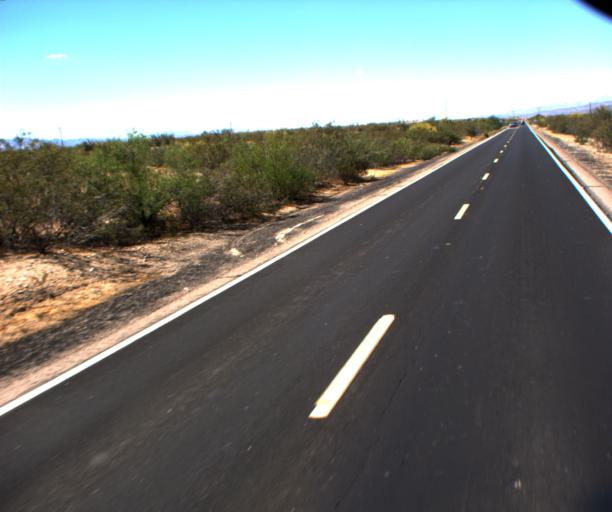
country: US
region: Arizona
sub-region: Yavapai County
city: Bagdad
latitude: 34.7259
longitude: -113.6150
